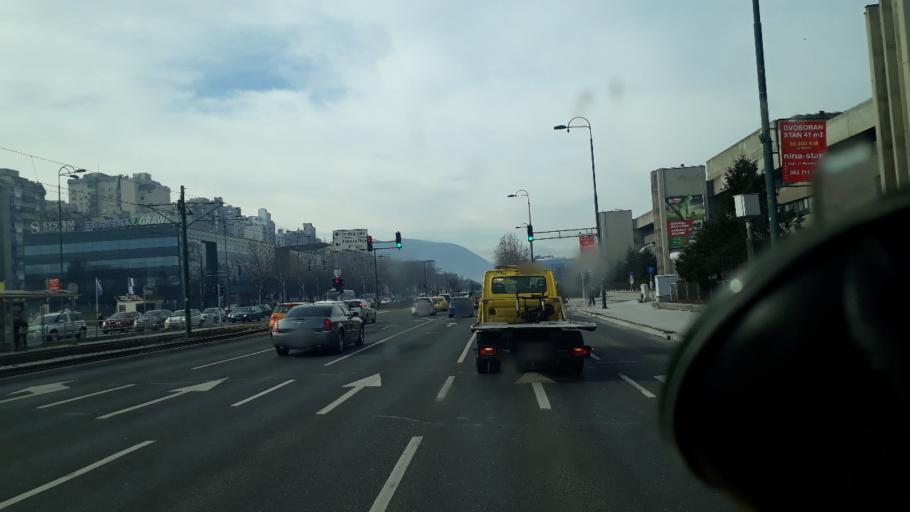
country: BA
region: Federation of Bosnia and Herzegovina
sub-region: Kanton Sarajevo
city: Sarajevo
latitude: 43.8448
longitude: 18.3555
